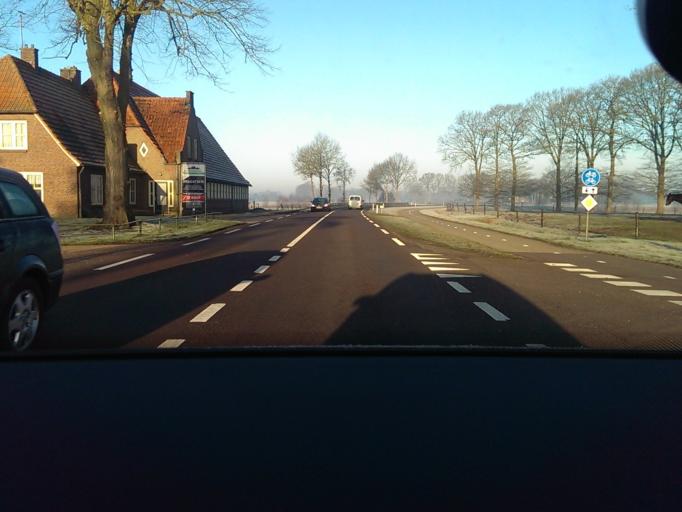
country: NL
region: Overijssel
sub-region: Gemeente Twenterand
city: Magele
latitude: 52.4439
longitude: 6.5297
